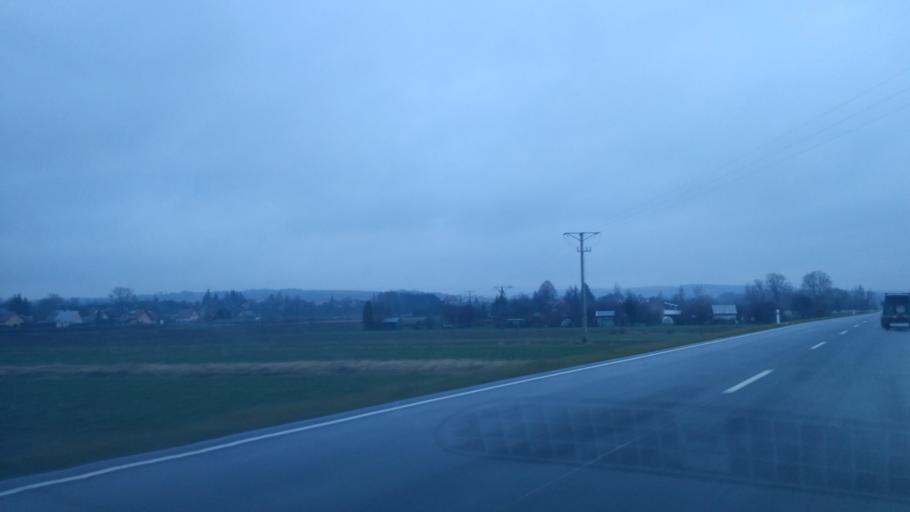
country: PL
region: Subcarpathian Voivodeship
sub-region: Powiat rzeszowski
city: Dynow
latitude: 49.8208
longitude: 22.2410
